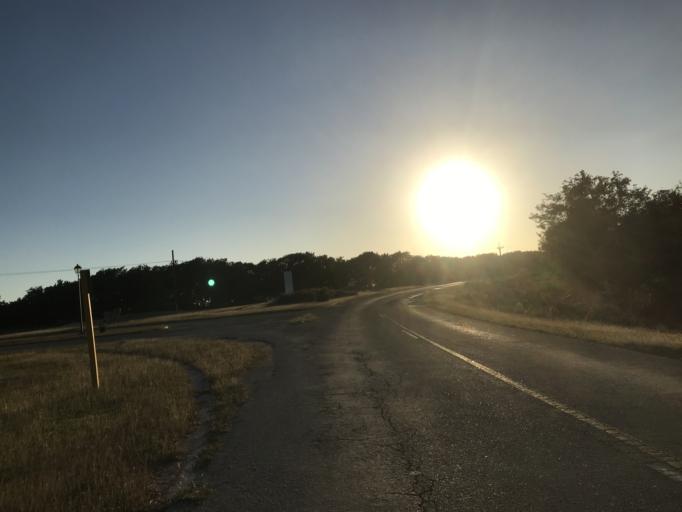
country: CU
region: Cienfuegos
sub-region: Municipio de Aguada de Pasajeros
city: Aguada de Pasajeros
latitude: 22.0673
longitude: -81.0412
